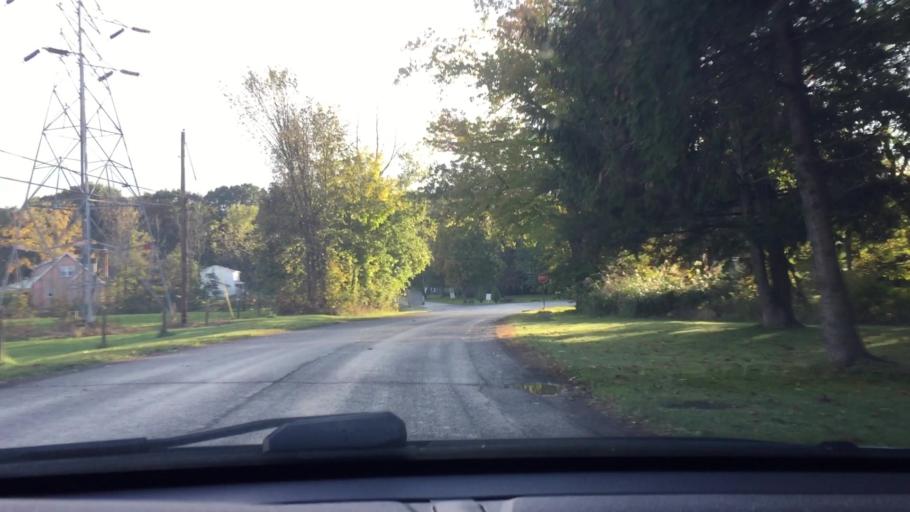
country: US
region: Pennsylvania
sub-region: Lawrence County
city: Bessemer
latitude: 41.0085
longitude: -80.4516
